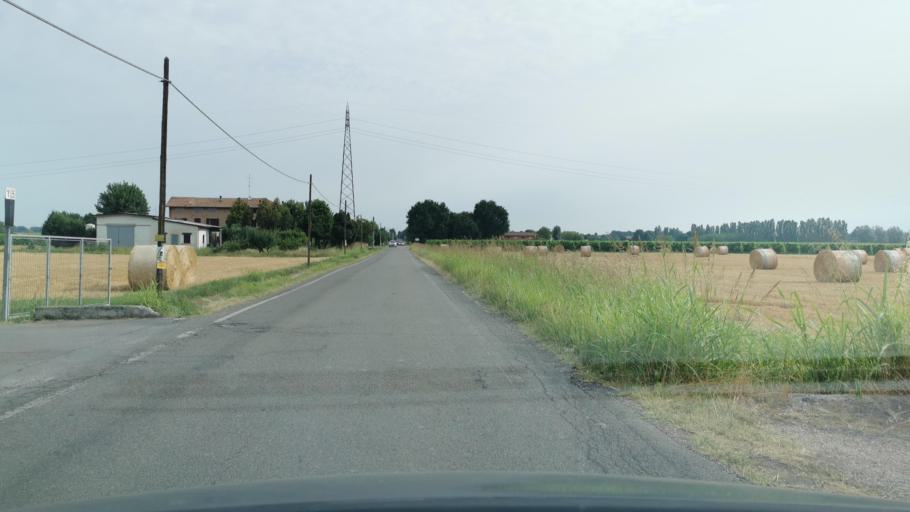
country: IT
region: Emilia-Romagna
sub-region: Provincia di Modena
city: Villanova
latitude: 44.6762
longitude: 10.9050
